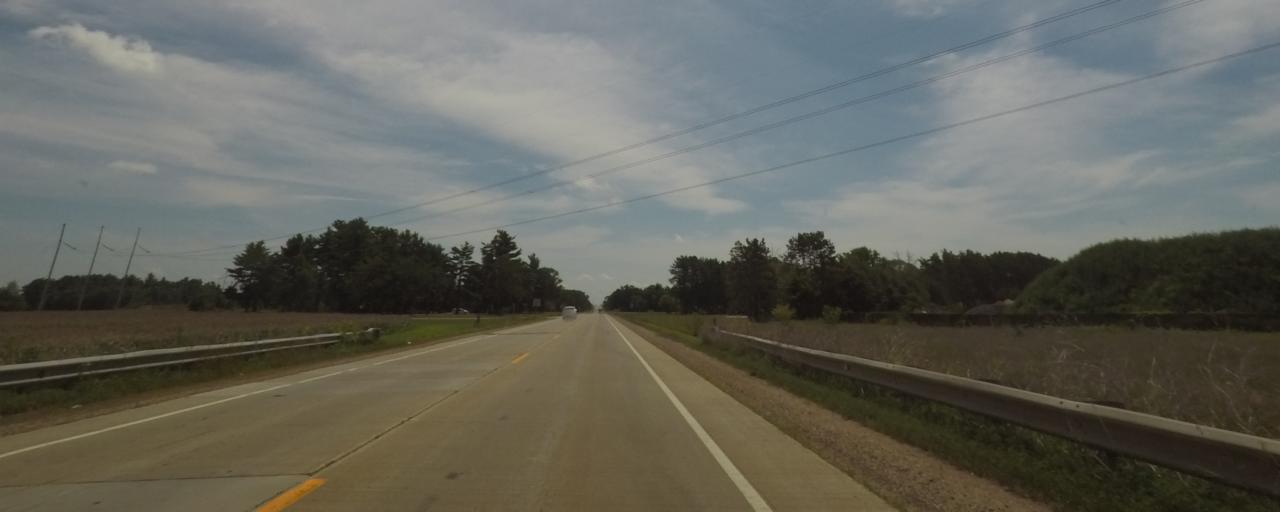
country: US
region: Wisconsin
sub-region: Portage County
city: Plover
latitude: 44.4399
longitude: -89.5321
